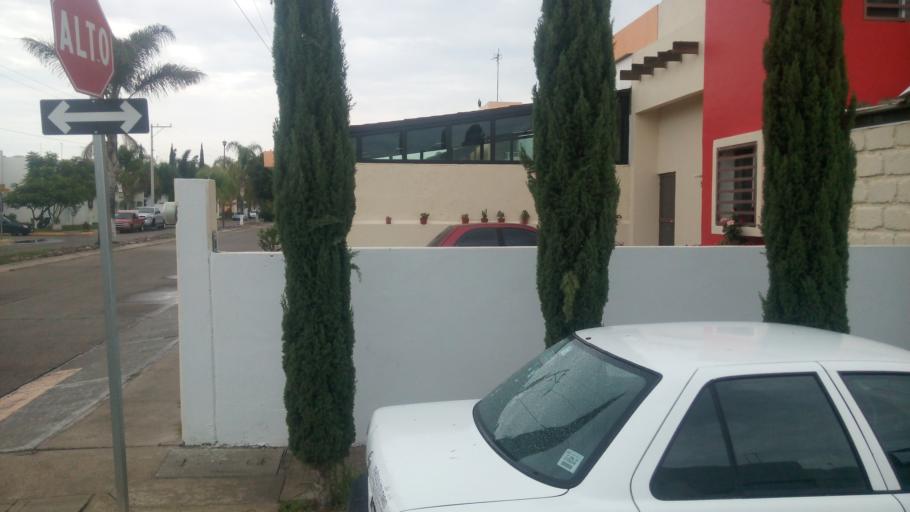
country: MX
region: Aguascalientes
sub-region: Aguascalientes
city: La Loma de los Negritos
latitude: 21.8434
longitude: -102.3312
